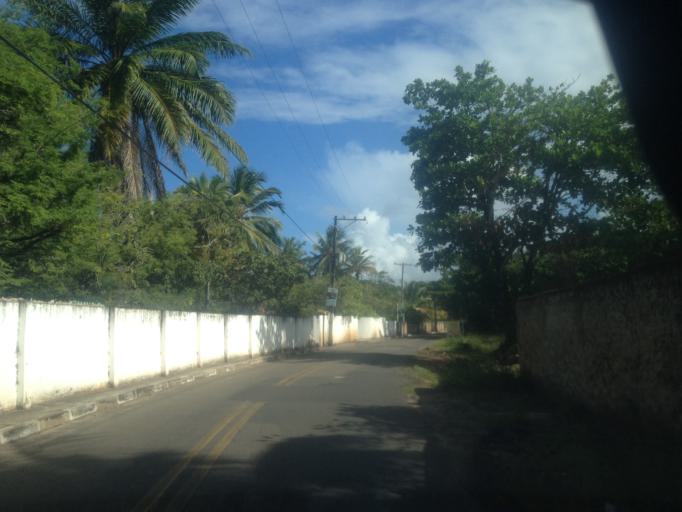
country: BR
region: Bahia
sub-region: Mata De Sao Joao
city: Mata de Sao Joao
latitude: -12.6172
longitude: -38.0442
